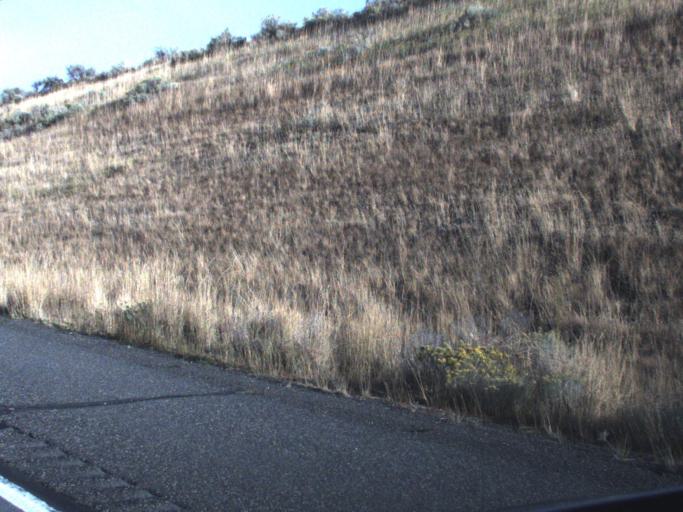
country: US
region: Oregon
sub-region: Umatilla County
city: Umatilla
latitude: 45.9981
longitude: -119.2650
